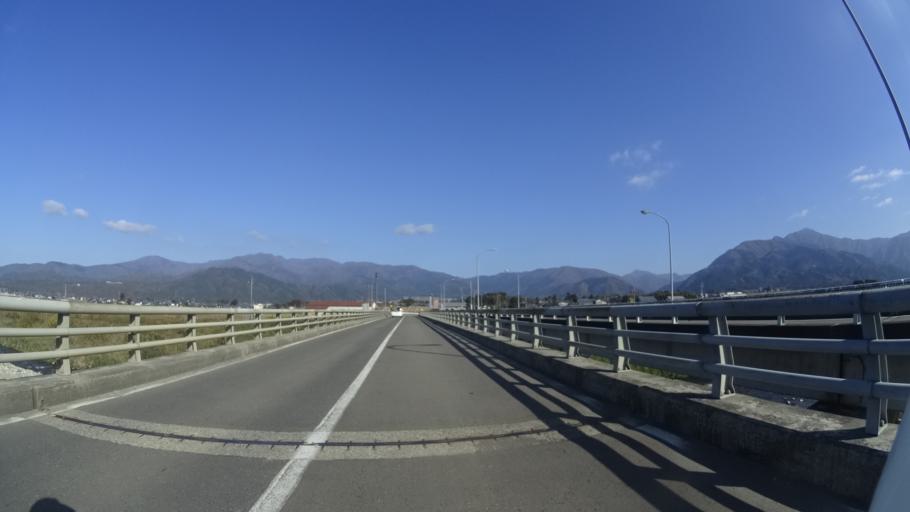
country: JP
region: Fukui
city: Ono
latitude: 35.9797
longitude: 136.5211
